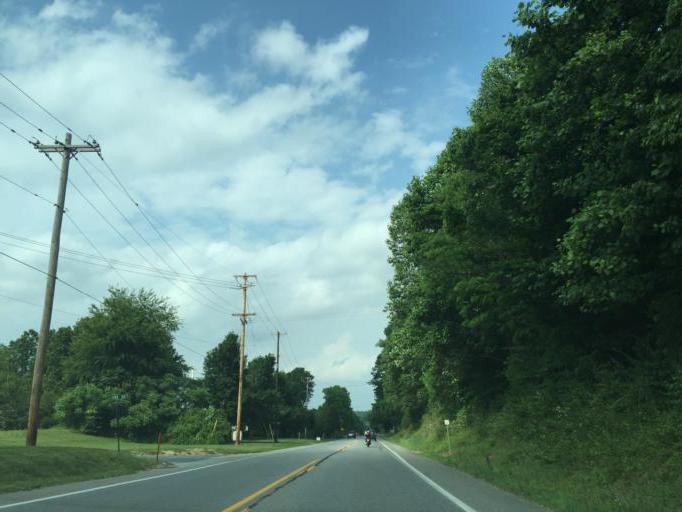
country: US
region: Pennsylvania
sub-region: York County
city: Susquehanna Trails
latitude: 39.7302
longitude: -76.3427
